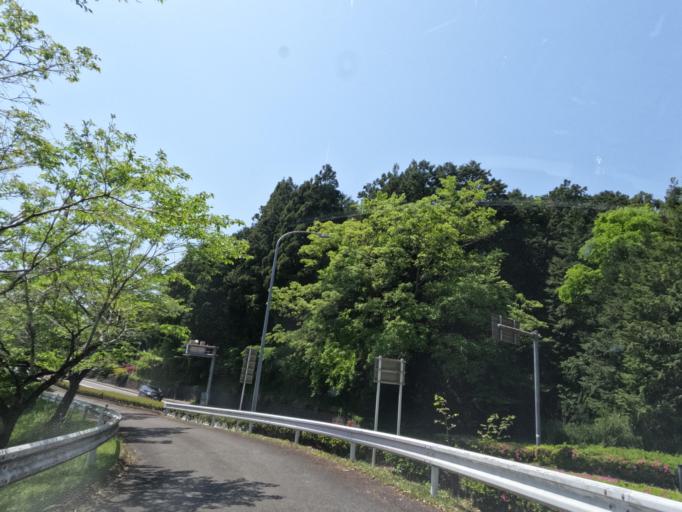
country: JP
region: Gifu
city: Tarui
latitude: 35.2962
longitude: 136.4750
